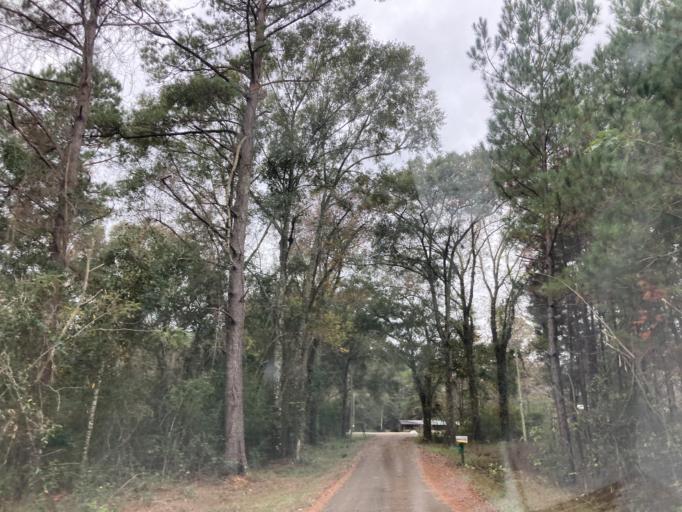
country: US
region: Mississippi
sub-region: Lamar County
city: Lumberton
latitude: 31.0900
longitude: -89.5969
